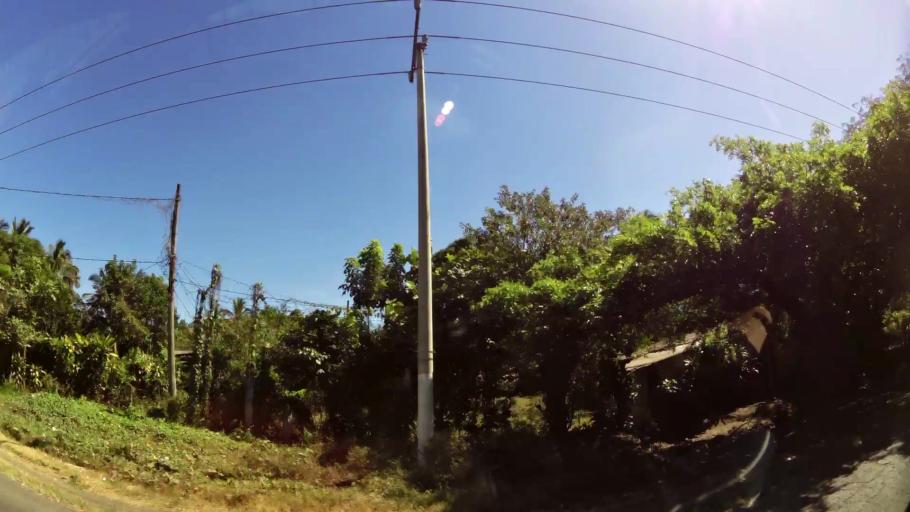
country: SV
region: La Libertad
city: San Juan Opico
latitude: 13.8566
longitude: -89.3592
